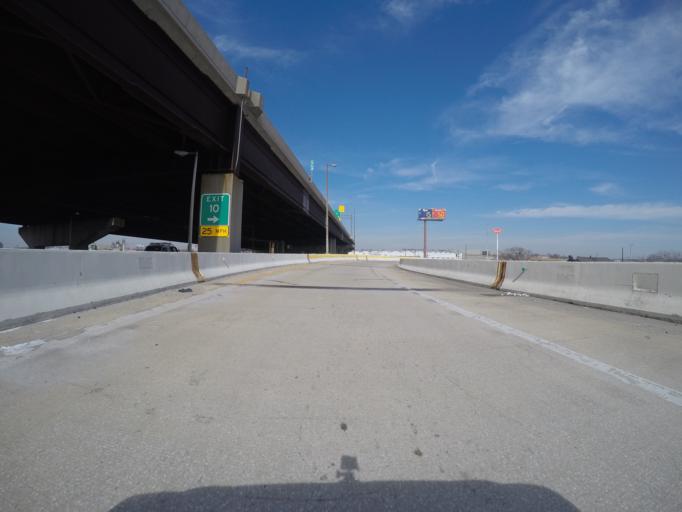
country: US
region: Maryland
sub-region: Baltimore County
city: Dundalk
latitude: 39.2701
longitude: -76.5565
